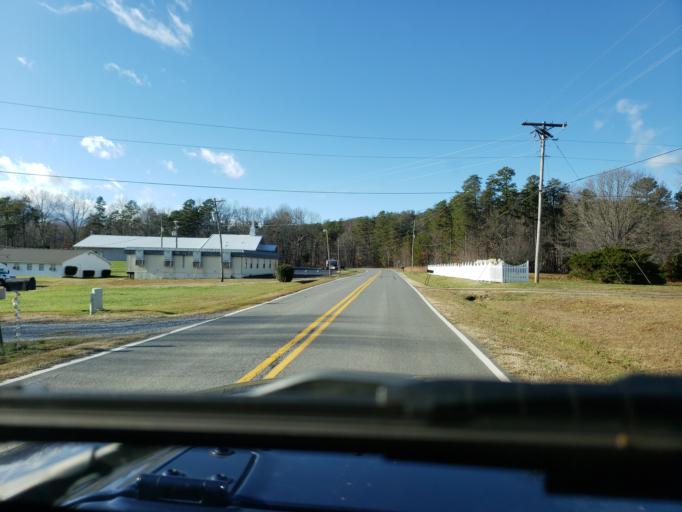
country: US
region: North Carolina
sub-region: Cleveland County
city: White Plains
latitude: 35.1697
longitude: -81.3569
